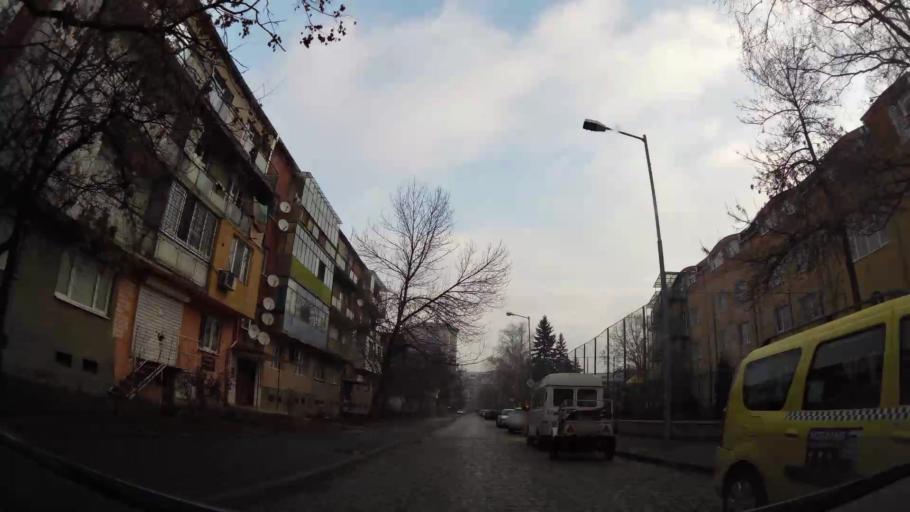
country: BG
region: Sofia-Capital
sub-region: Stolichna Obshtina
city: Sofia
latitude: 42.7312
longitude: 23.3099
